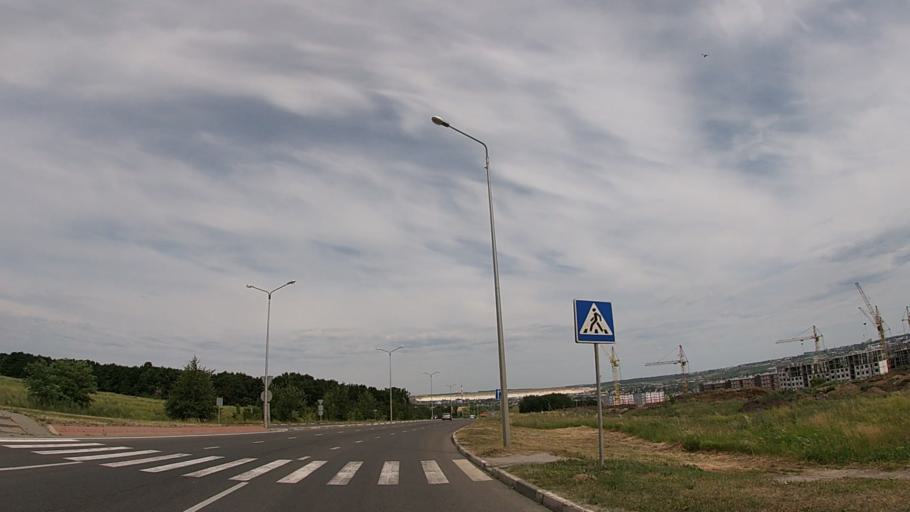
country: RU
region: Belgorod
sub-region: Belgorodskiy Rayon
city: Belgorod
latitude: 50.5941
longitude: 36.5311
